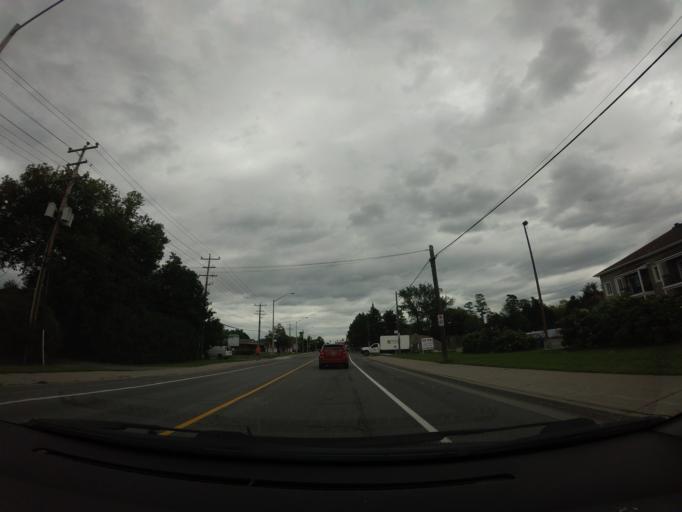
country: CA
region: Ontario
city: Ottawa
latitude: 45.4302
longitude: -75.5682
